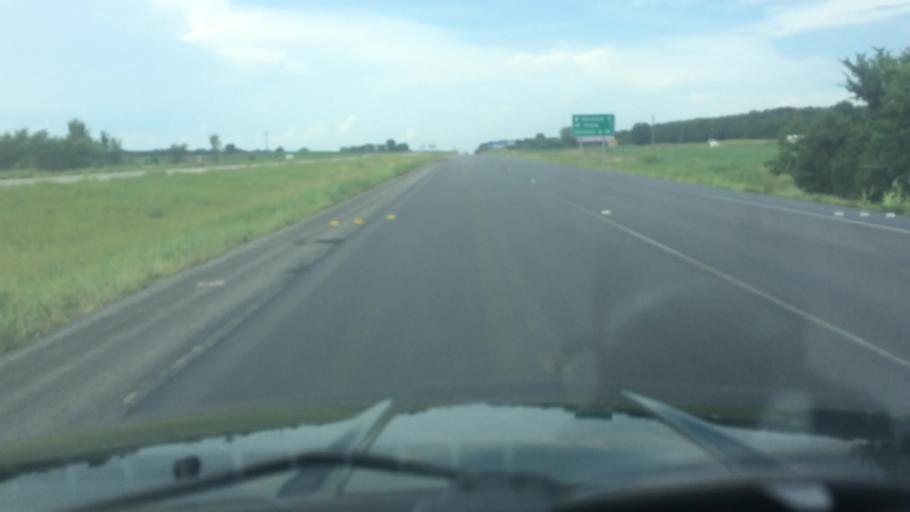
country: US
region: Missouri
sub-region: Saint Clair County
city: Osceola
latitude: 37.9875
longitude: -93.6511
